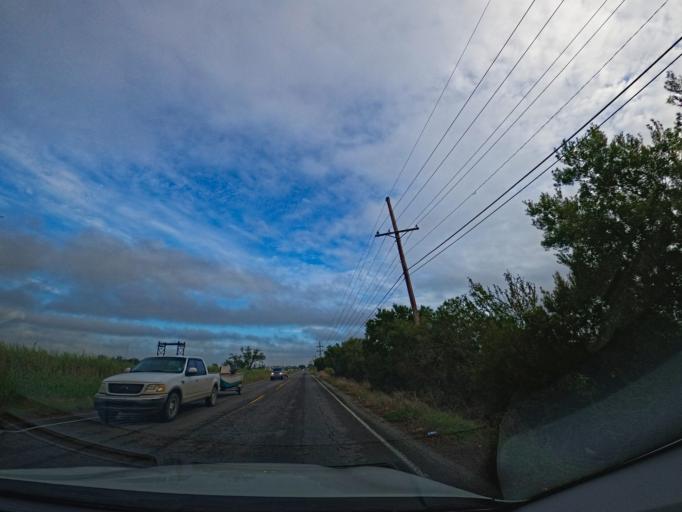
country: US
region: Louisiana
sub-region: Terrebonne Parish
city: Dulac
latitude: 29.3803
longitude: -90.7135
